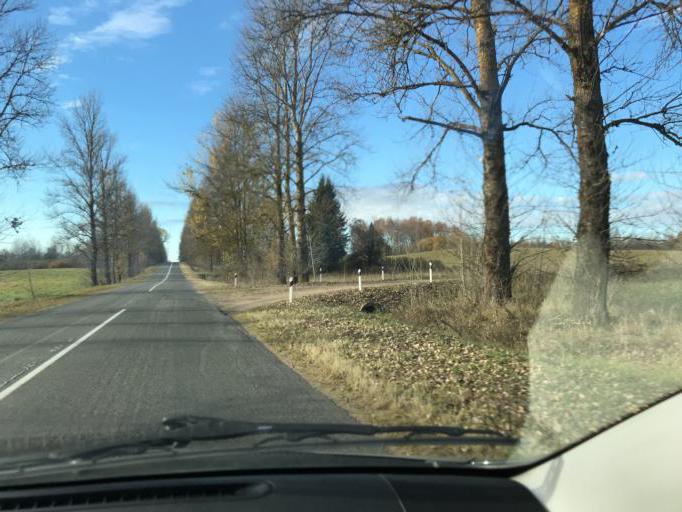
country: BY
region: Vitebsk
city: Haradok
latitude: 55.3549
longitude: 29.5774
